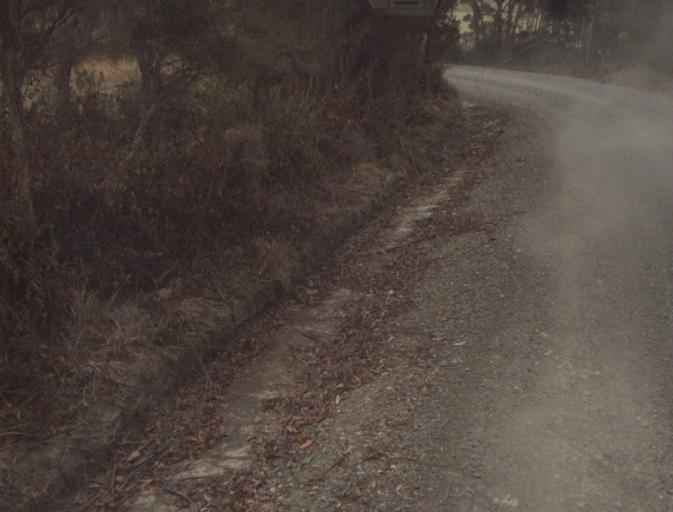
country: AU
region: Tasmania
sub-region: Launceston
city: Mayfield
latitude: -41.2414
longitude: 147.1650
